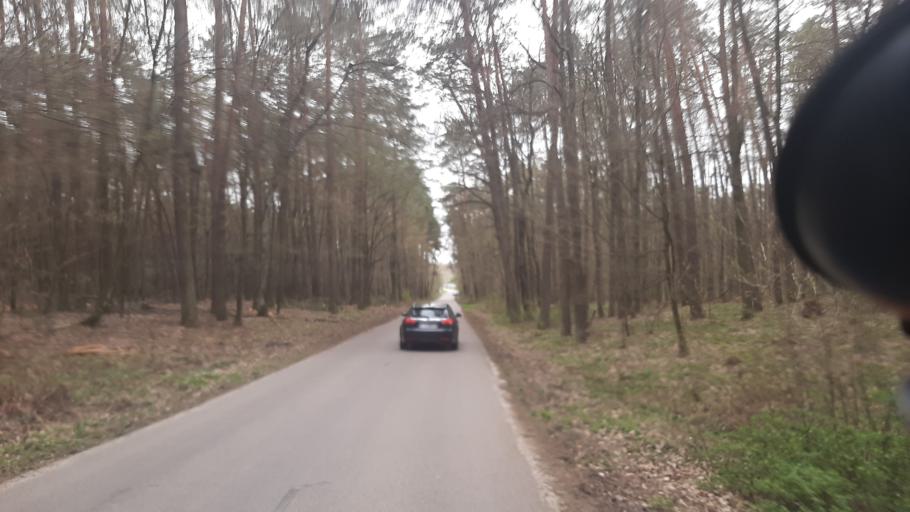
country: PL
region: Lublin Voivodeship
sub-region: Powiat lubelski
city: Niemce
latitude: 51.3714
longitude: 22.5525
